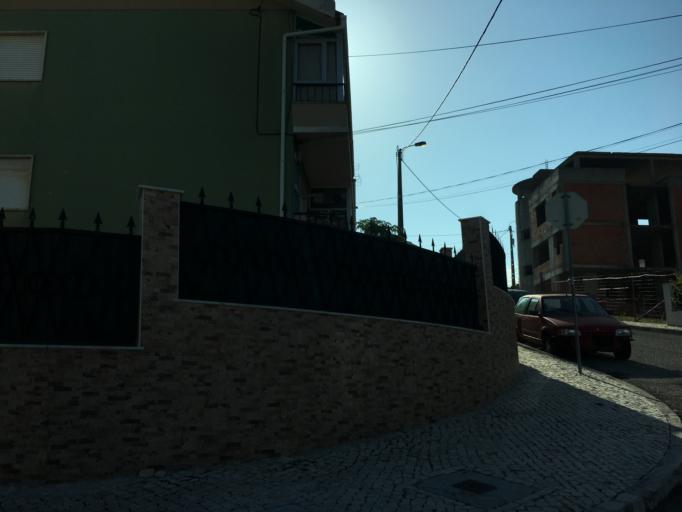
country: PT
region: Lisbon
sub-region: Cascais
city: Sao Domingos de Rana
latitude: 38.7099
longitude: -9.3449
